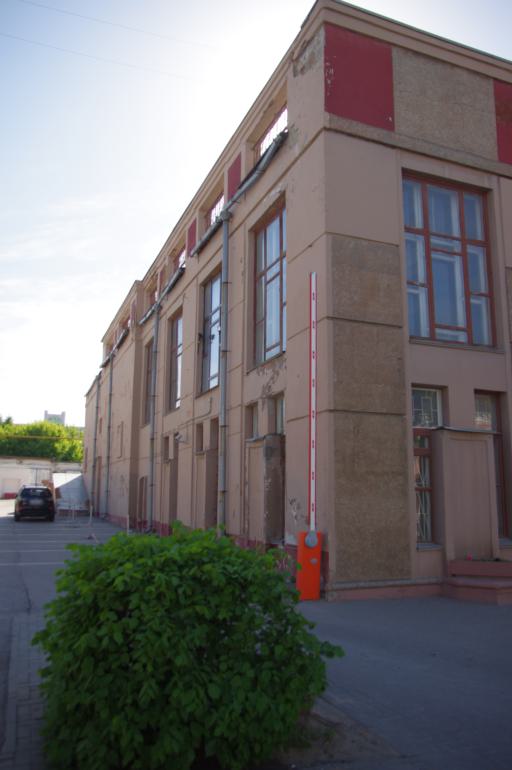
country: RU
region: Rjazan
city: Ryazan'
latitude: 54.6271
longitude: 39.7474
